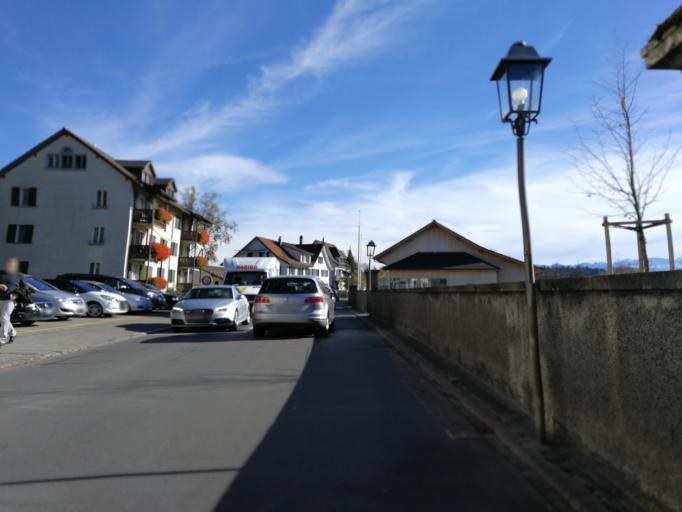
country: CH
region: Zurich
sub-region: Bezirk Hinwil
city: Binzikon
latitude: 47.2842
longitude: 8.7641
